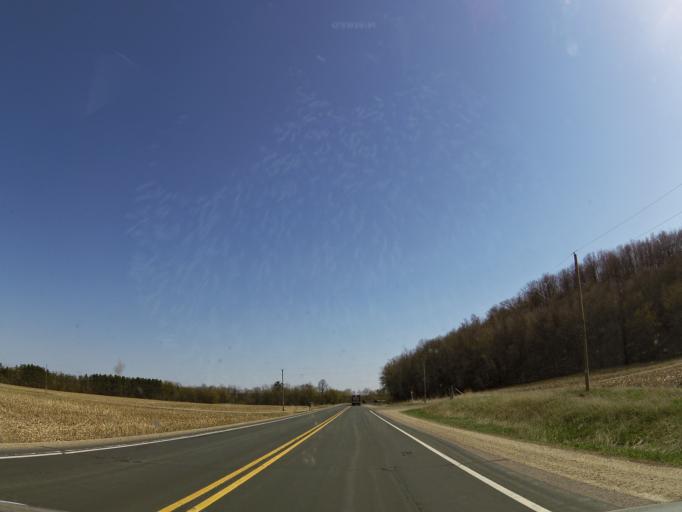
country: US
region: Wisconsin
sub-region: Dunn County
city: Menomonie
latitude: 44.7527
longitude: -91.9308
